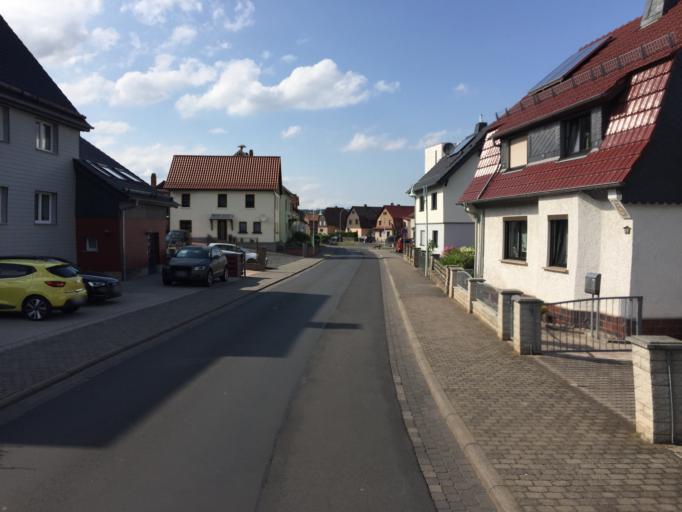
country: DE
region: Thuringia
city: Immelborn
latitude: 50.7941
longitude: 10.2768
